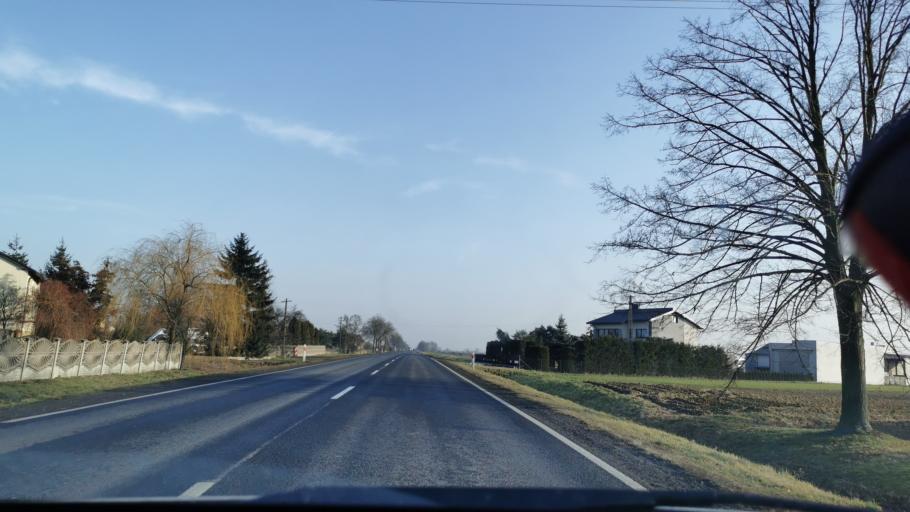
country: PL
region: Lodz Voivodeship
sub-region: Powiat sieradzki
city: Blaszki
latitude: 51.6725
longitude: 18.3672
